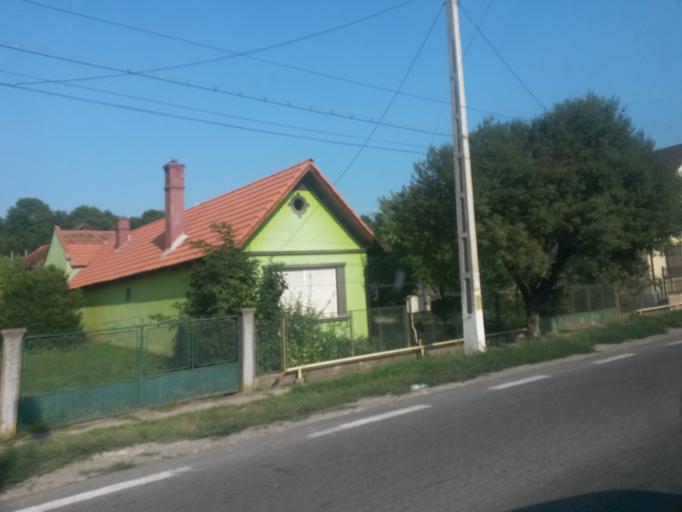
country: RO
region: Alba
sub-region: Comuna Unirea
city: Unirea
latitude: 46.4086
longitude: 23.8099
